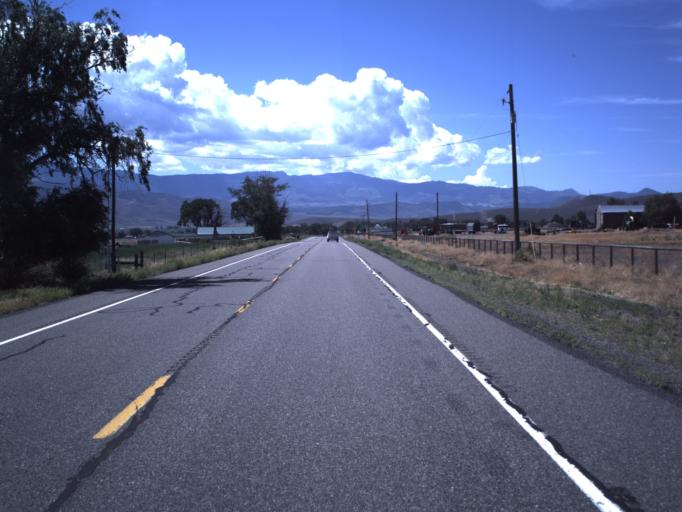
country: US
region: Utah
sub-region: Piute County
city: Junction
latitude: 38.2553
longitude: -112.2205
